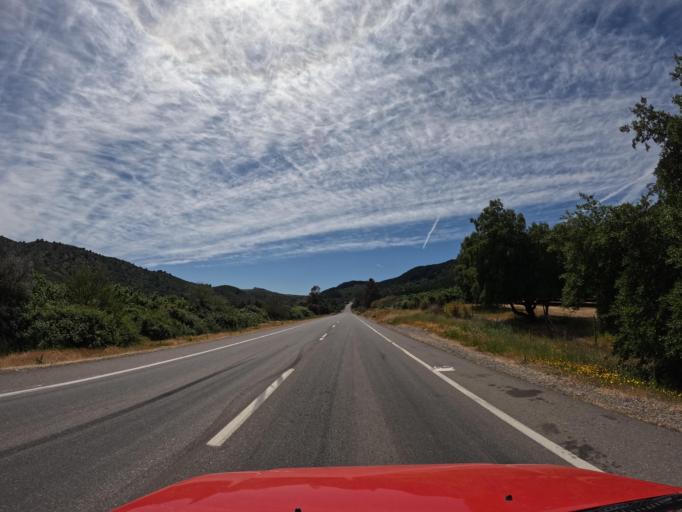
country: CL
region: Maule
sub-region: Provincia de Talca
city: Talca
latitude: -35.2526
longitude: -71.5427
